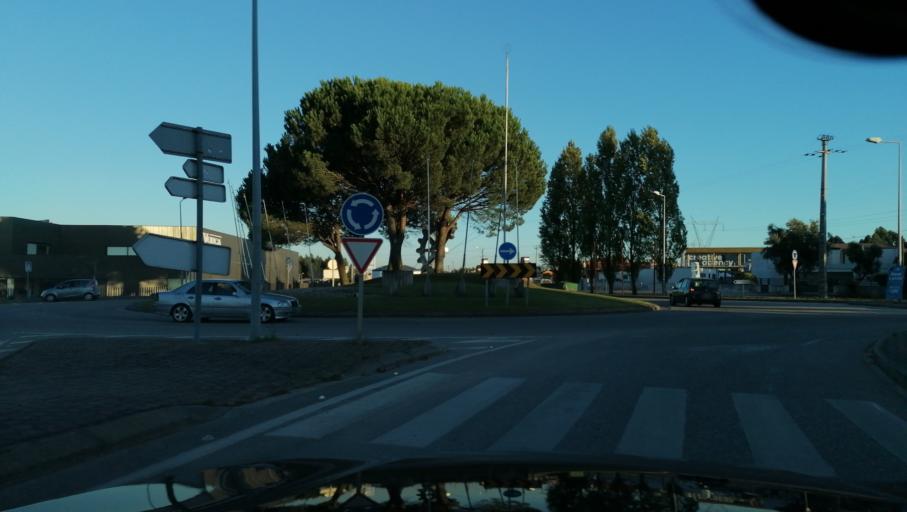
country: PT
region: Aveiro
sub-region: Agueda
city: Agueda
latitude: 40.5567
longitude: -8.4656
